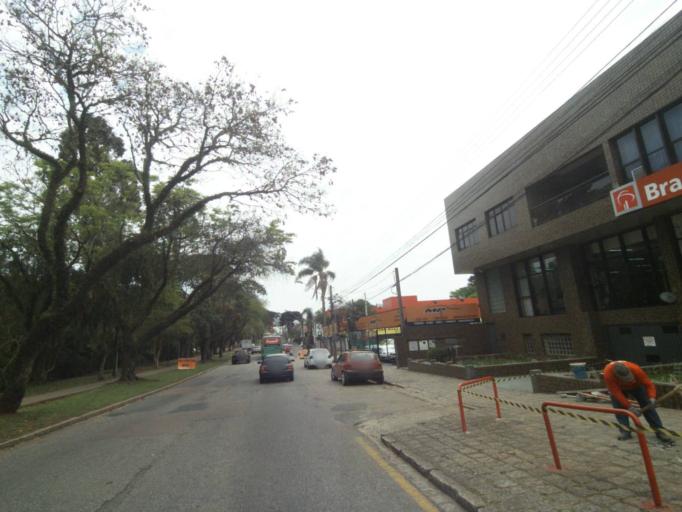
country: BR
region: Parana
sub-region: Curitiba
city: Curitiba
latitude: -25.4548
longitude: -49.3036
